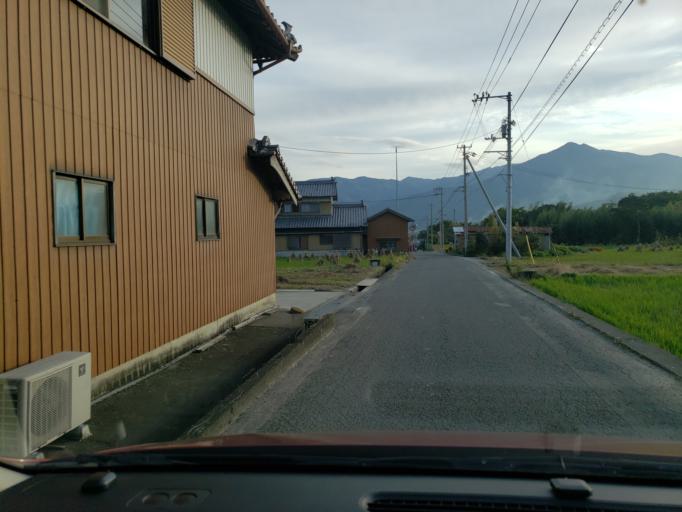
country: JP
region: Tokushima
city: Wakimachi
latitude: 34.0793
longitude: 134.2284
